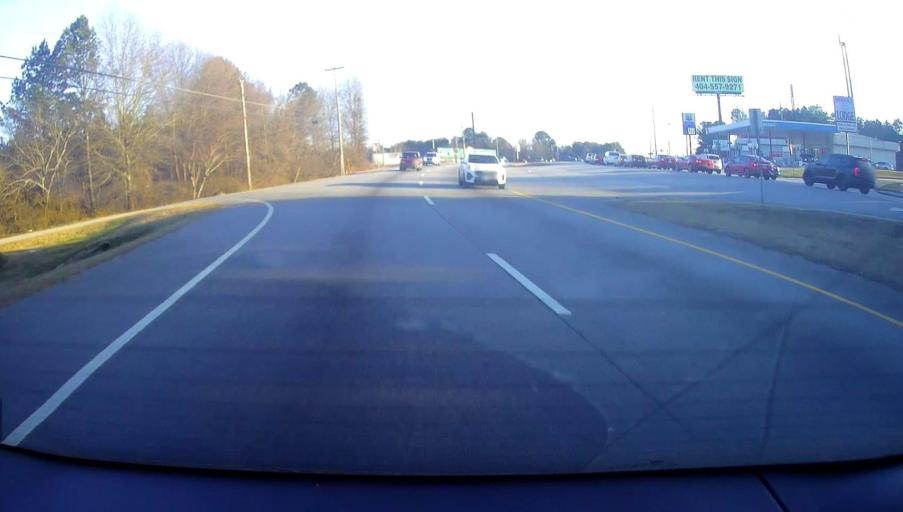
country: US
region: Georgia
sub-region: Fulton County
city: Fairburn
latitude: 33.5494
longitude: -84.5778
